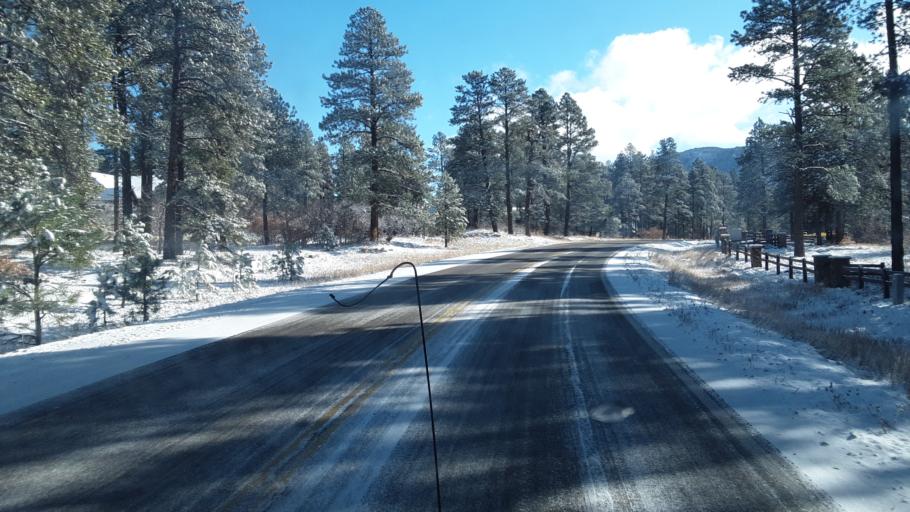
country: US
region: Colorado
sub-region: La Plata County
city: Durango
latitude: 37.3125
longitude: -107.7901
